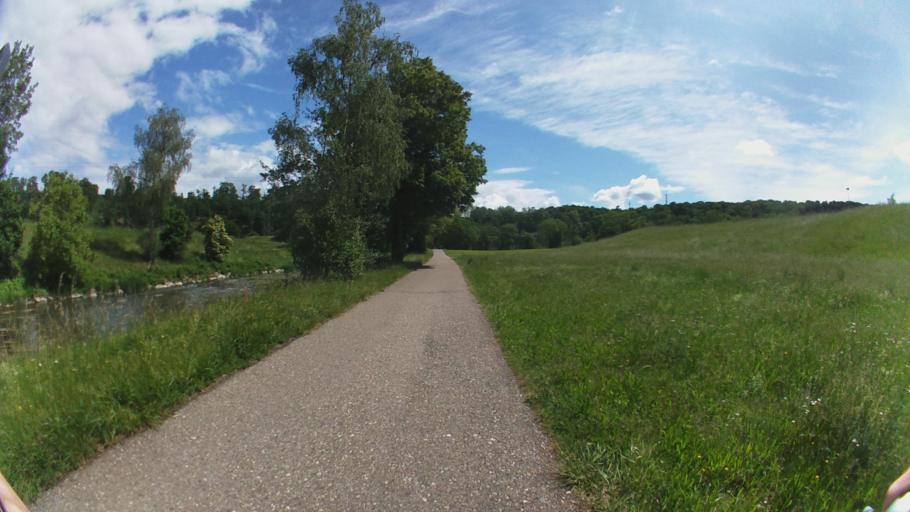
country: CH
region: Zurich
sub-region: Bezirk Buelach
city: Glattfelden
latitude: 47.5495
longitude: 8.5193
